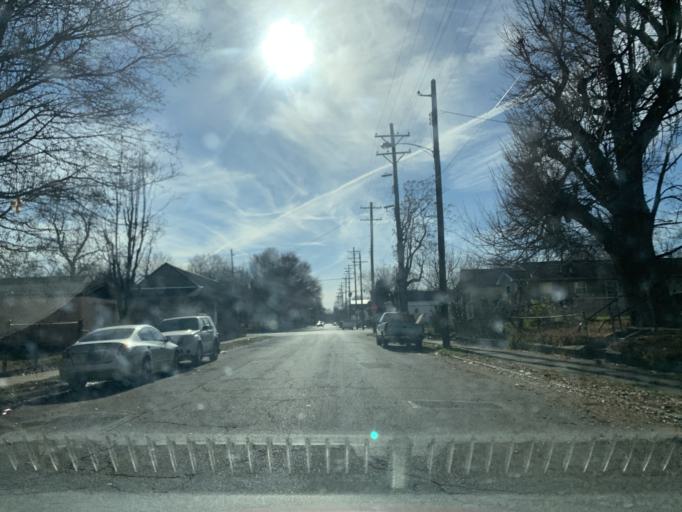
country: US
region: Kentucky
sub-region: Jefferson County
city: Louisville
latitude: 38.2629
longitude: -85.7824
